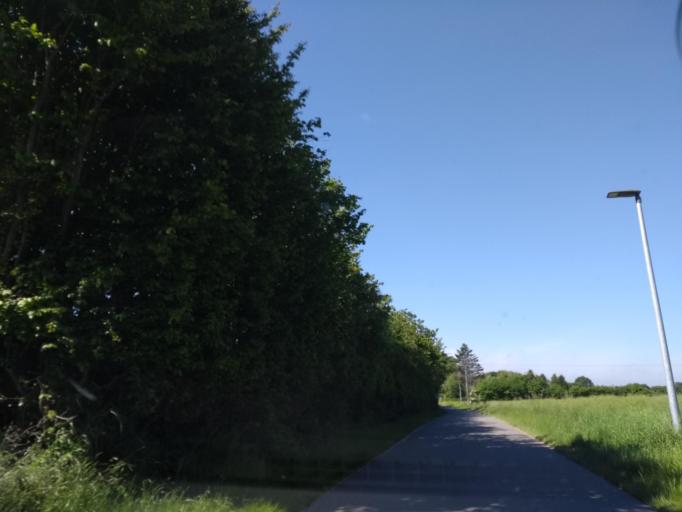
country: DE
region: Schleswig-Holstein
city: Waabs
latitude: 54.5524
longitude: 9.9860
